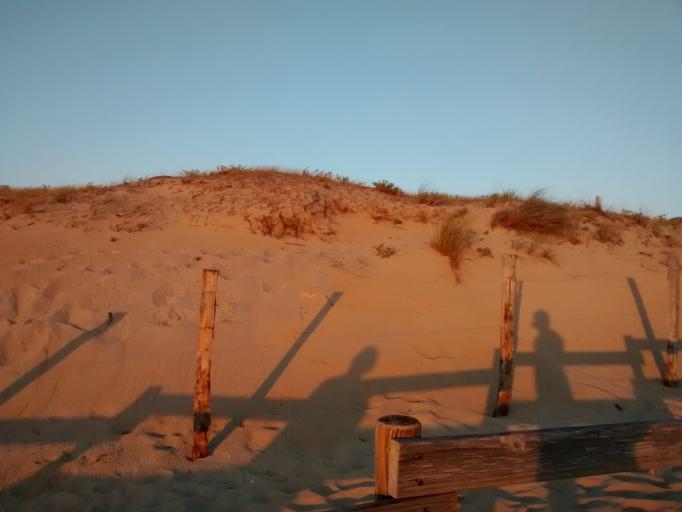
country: FR
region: Aquitaine
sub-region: Departement des Landes
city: Vieux-Boucau-les-Bains
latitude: 43.8163
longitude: -1.4049
